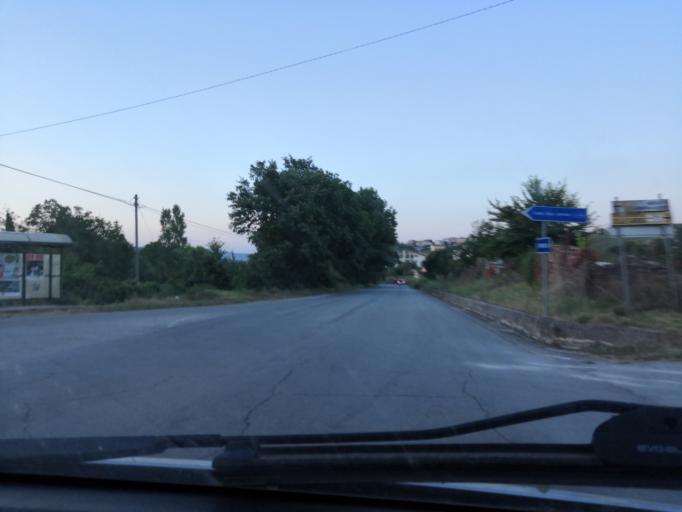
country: IT
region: Molise
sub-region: Provincia di Campobasso
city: Jelsi
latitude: 41.5104
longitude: 14.7874
